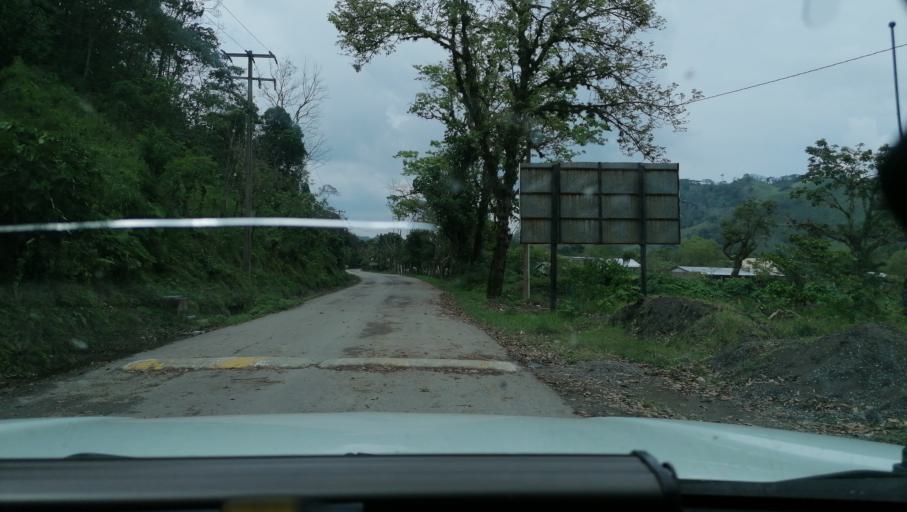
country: MX
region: Chiapas
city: Ixtacomitan
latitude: 17.3336
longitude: -93.1300
